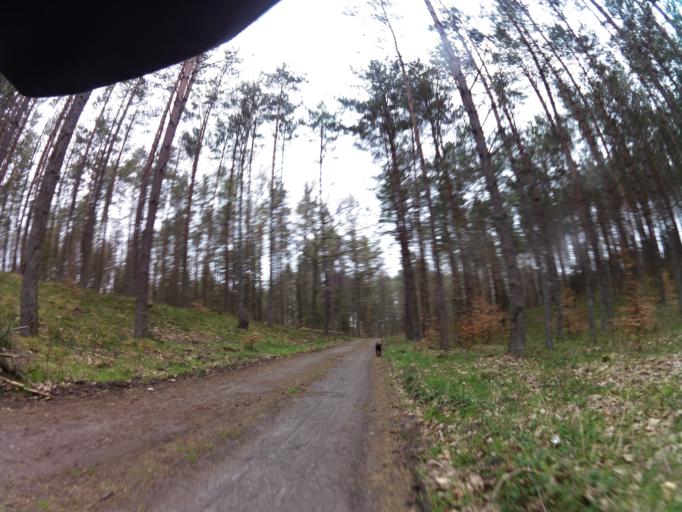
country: PL
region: West Pomeranian Voivodeship
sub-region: Powiat koszalinski
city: Bobolice
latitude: 53.9418
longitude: 16.6858
